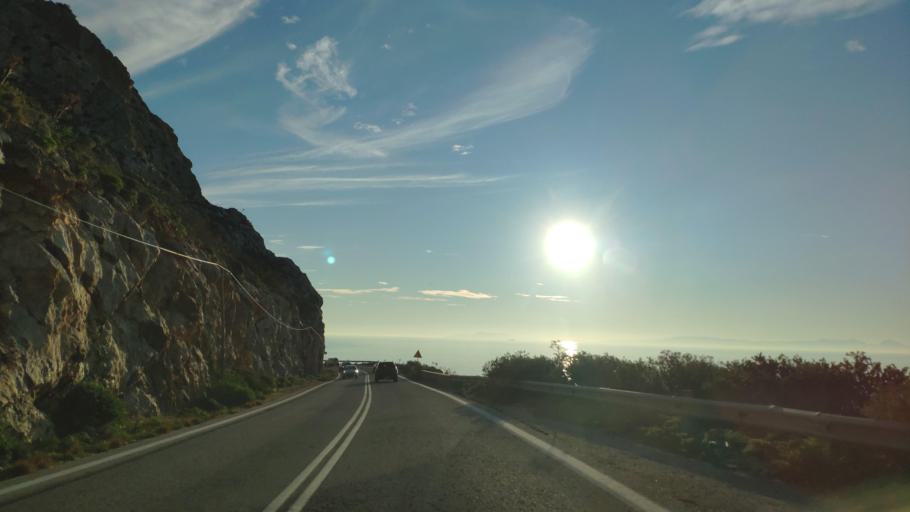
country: GR
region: Attica
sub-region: Nomarchia Anatolikis Attikis
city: Palaia Fokaia
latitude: 37.6748
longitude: 23.9395
